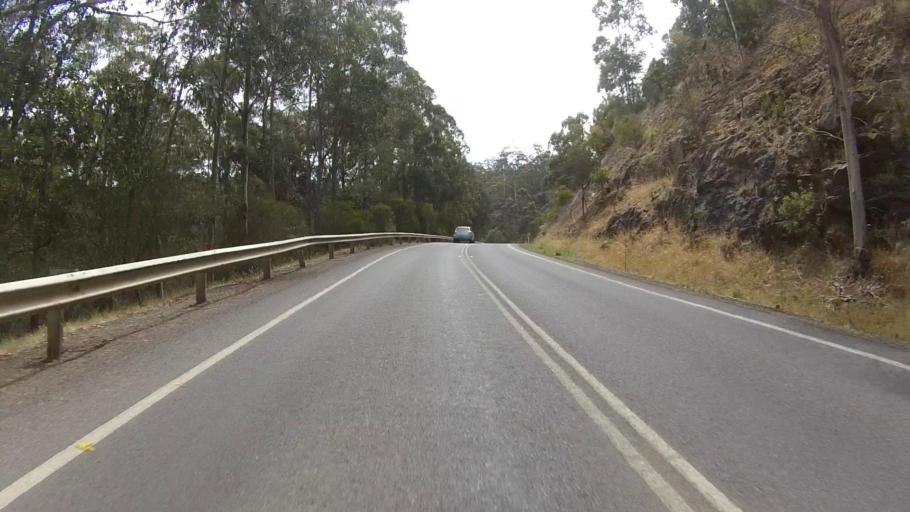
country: AU
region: Tasmania
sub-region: Kingborough
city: Kettering
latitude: -43.1031
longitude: 147.2450
